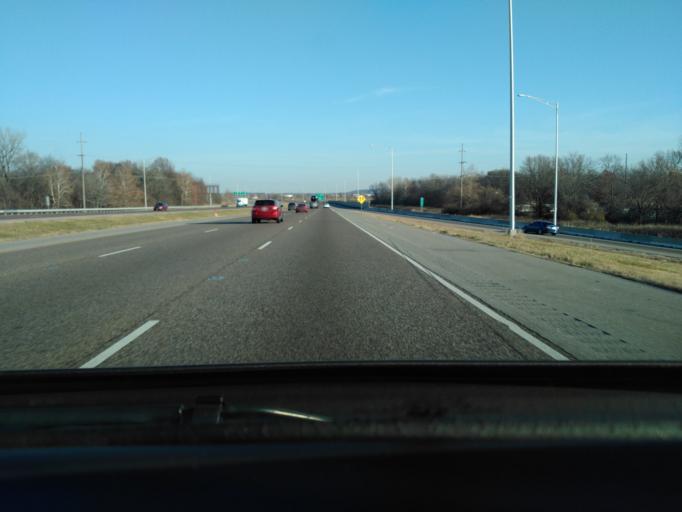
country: US
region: Illinois
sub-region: Saint Clair County
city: Caseyville
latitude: 38.6610
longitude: -90.0304
